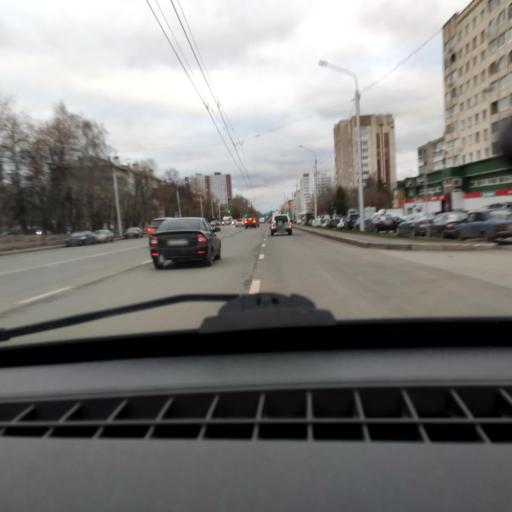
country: RU
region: Bashkortostan
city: Ufa
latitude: 54.7786
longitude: 56.0362
